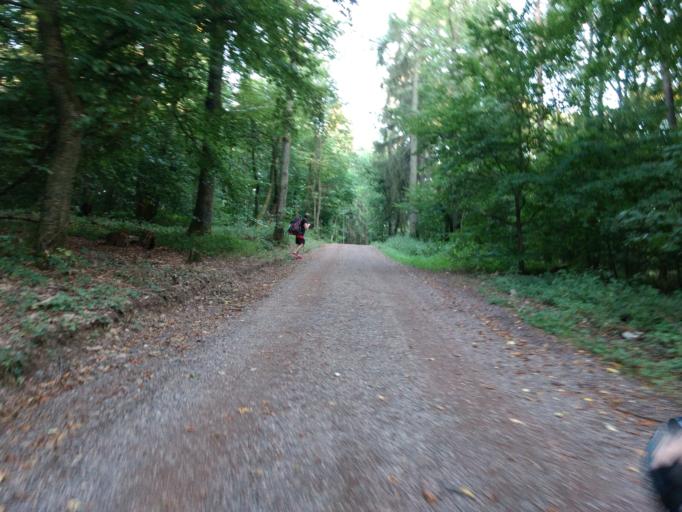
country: DE
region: Saarland
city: Nalbach
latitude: 49.4026
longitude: 6.7836
